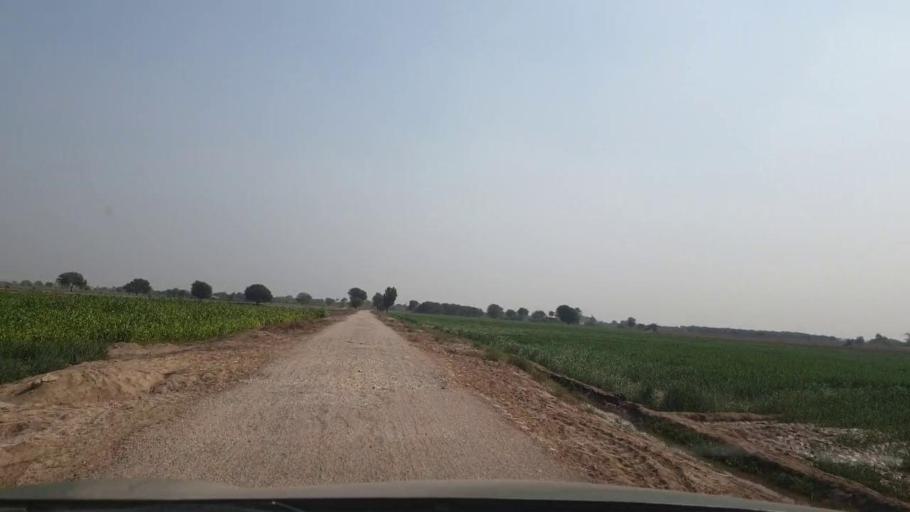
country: PK
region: Sindh
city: Tando Allahyar
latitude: 25.5634
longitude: 68.8228
